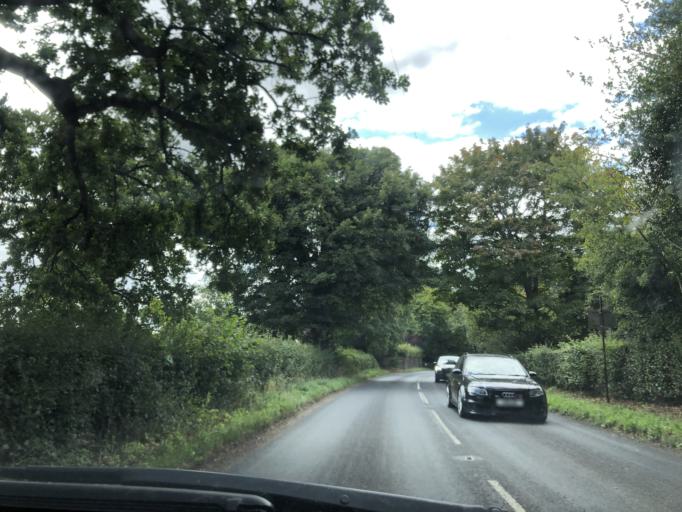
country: GB
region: England
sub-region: Kent
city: Westerham
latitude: 51.2300
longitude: 0.0615
